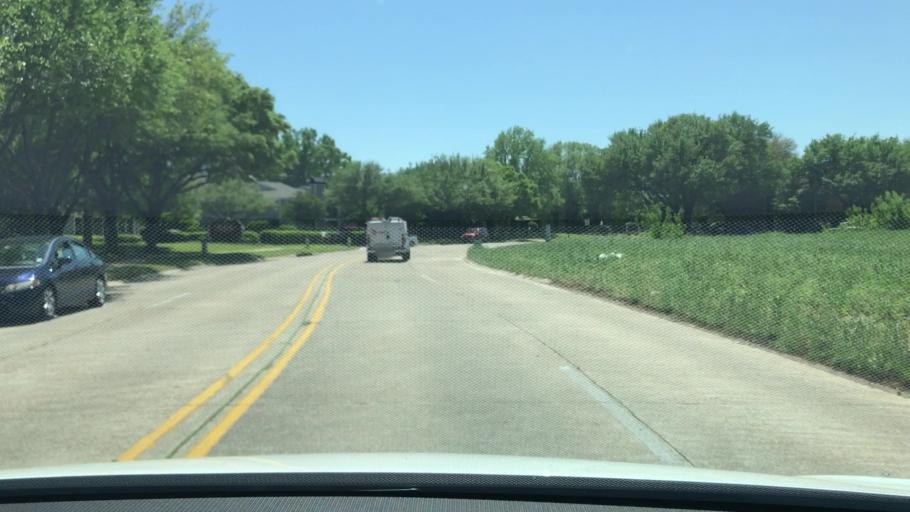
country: US
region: Louisiana
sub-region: Bossier Parish
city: Bossier City
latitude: 32.4255
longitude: -93.7103
